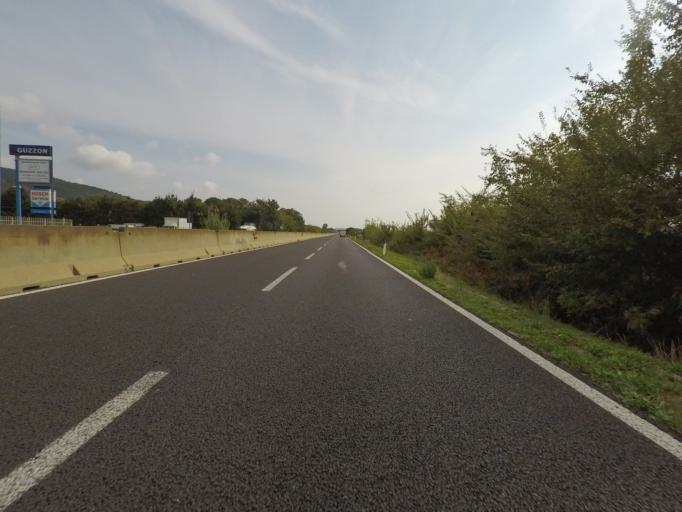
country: IT
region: Tuscany
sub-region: Provincia di Grosseto
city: Orbetello Scalo
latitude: 42.4655
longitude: 11.2412
